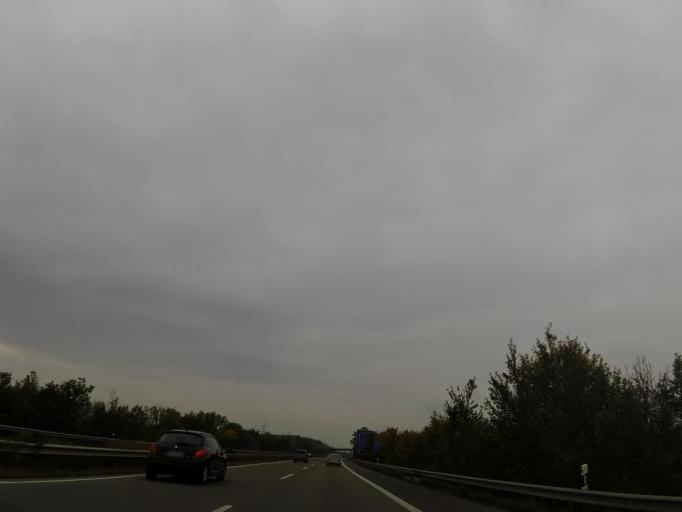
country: DE
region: Rheinland-Pfalz
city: Albig
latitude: 49.7843
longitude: 8.1288
